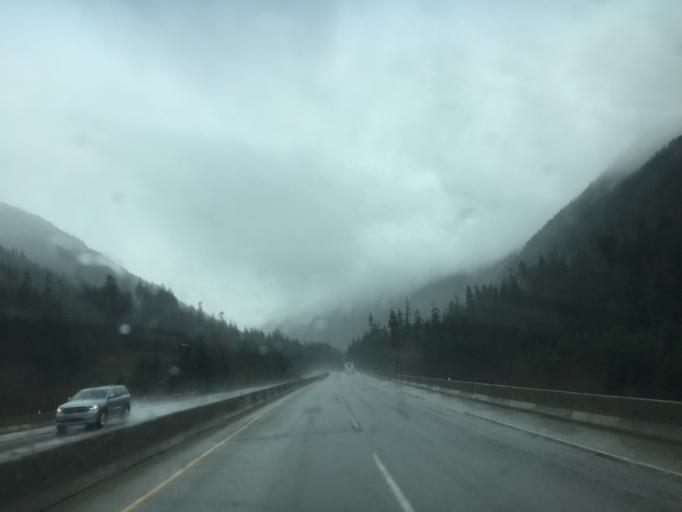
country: CA
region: British Columbia
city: Hope
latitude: 49.5489
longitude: -121.1942
